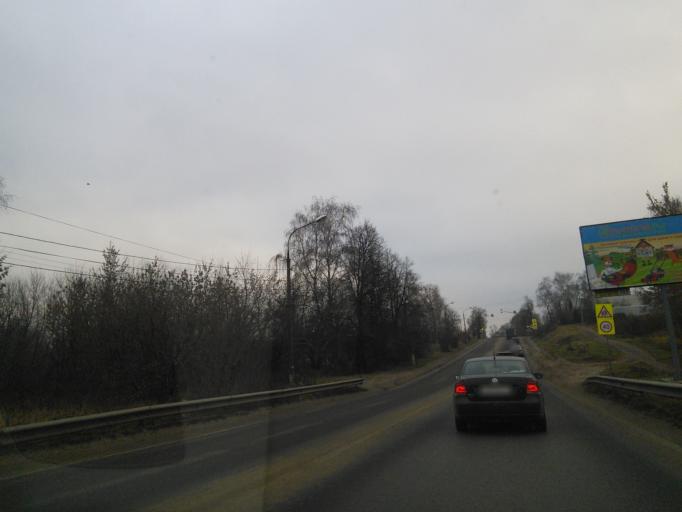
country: RU
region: Moskovskaya
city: Tomilino
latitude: 55.6326
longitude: 37.9452
